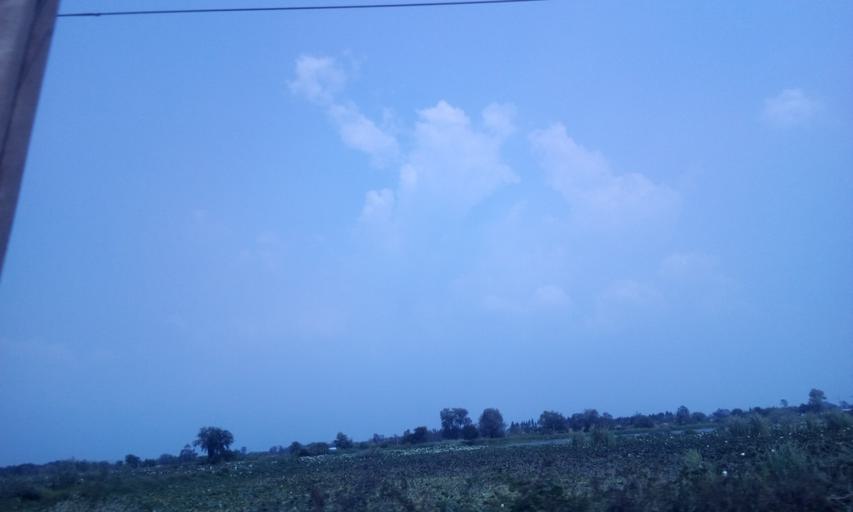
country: TH
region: Chon Buri
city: Phanat Nikhom
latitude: 13.4775
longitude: 101.1692
